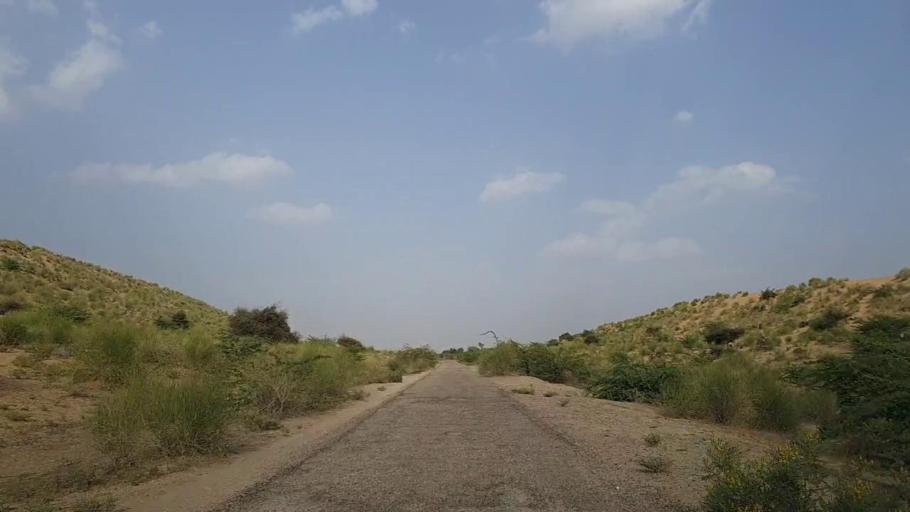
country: PK
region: Sindh
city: Islamkot
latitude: 24.7707
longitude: 70.1782
